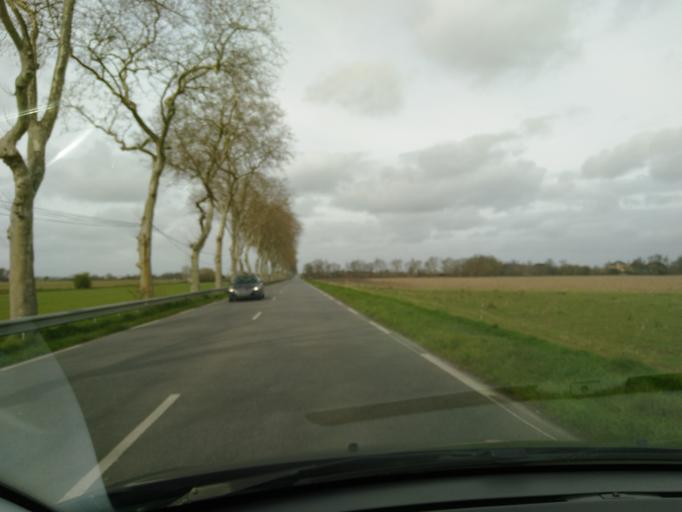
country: FR
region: Midi-Pyrenees
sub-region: Departement de la Haute-Garonne
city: Merville
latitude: 43.7276
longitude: 1.3234
